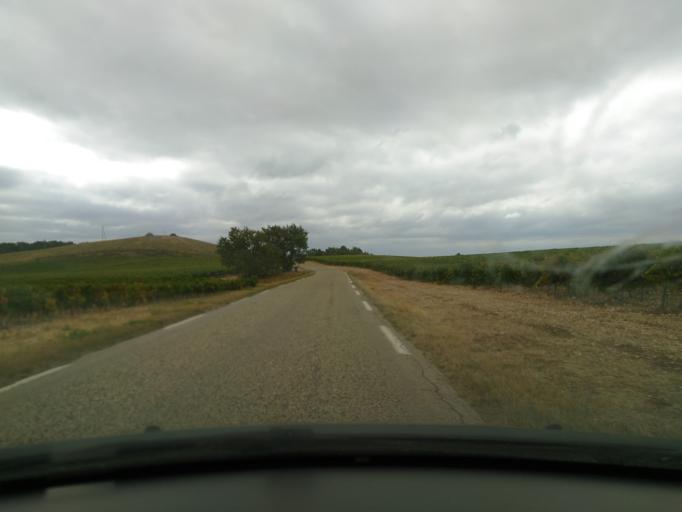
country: FR
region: Provence-Alpes-Cote d'Azur
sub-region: Departement du Vaucluse
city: Valreas
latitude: 44.3634
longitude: 5.0205
